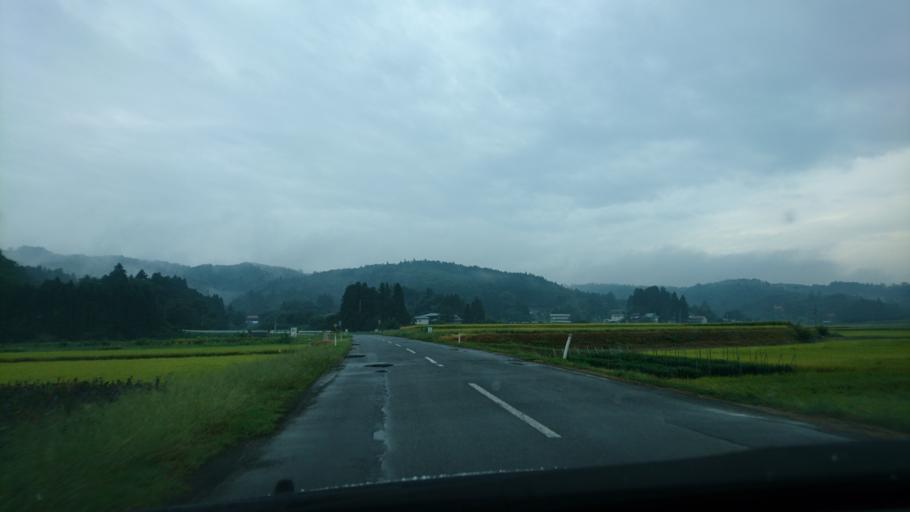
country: JP
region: Iwate
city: Ichinoseki
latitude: 38.8817
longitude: 141.2567
